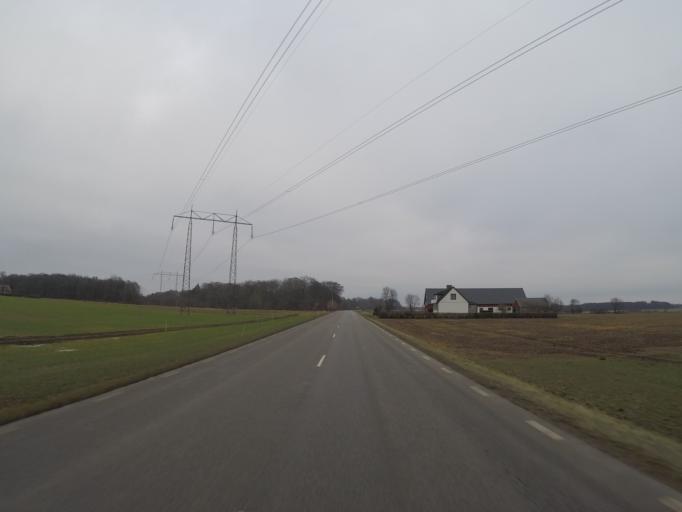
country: SE
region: Skane
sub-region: Hoors Kommun
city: Loberod
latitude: 55.7705
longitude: 13.4656
